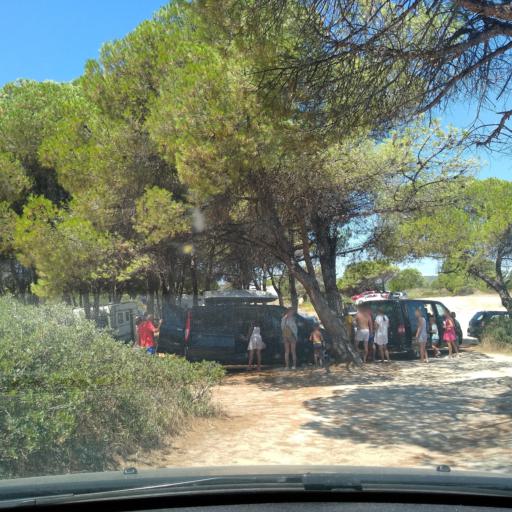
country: GR
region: Central Macedonia
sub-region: Nomos Chalkidikis
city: Neos Marmaras
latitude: 40.1936
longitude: 23.8063
